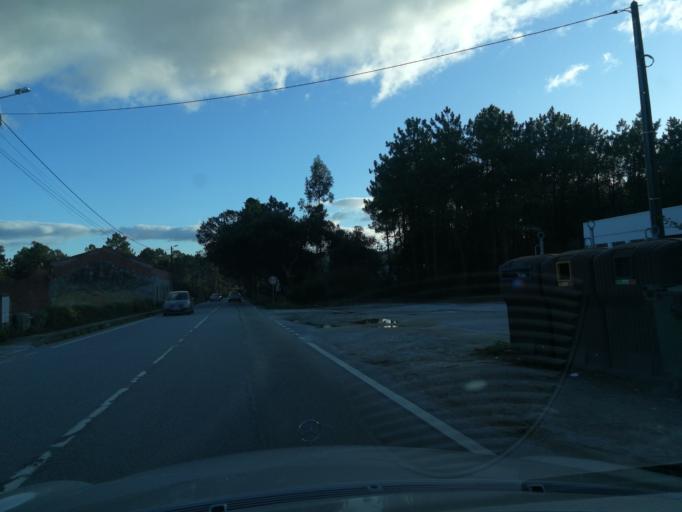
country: PT
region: Viana do Castelo
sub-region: Viana do Castelo
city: Darque
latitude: 41.6204
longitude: -8.7559
